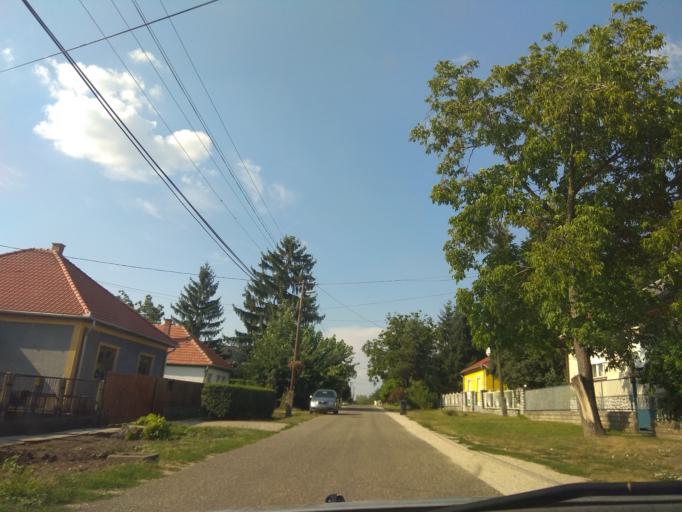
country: HU
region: Borsod-Abauj-Zemplen
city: Emod
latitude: 47.9345
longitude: 20.8152
